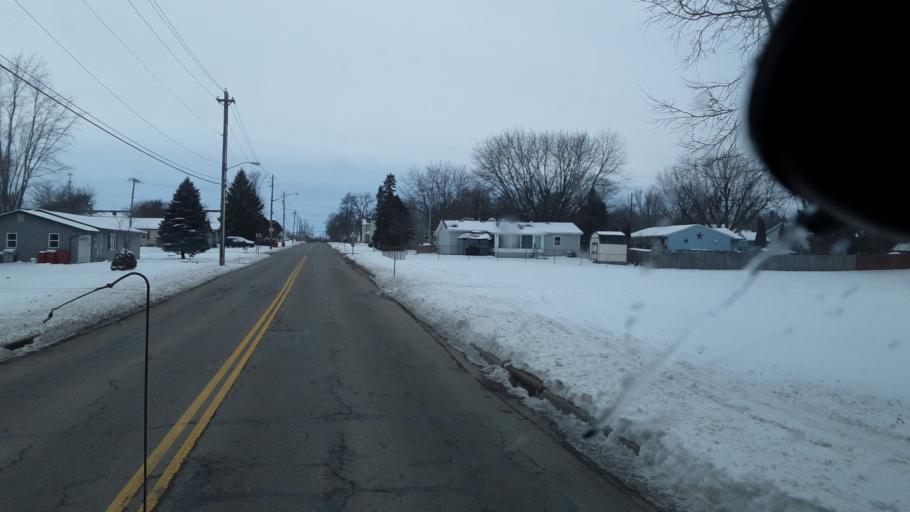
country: US
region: Ohio
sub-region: Madison County
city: London
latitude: 39.8790
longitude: -83.4519
